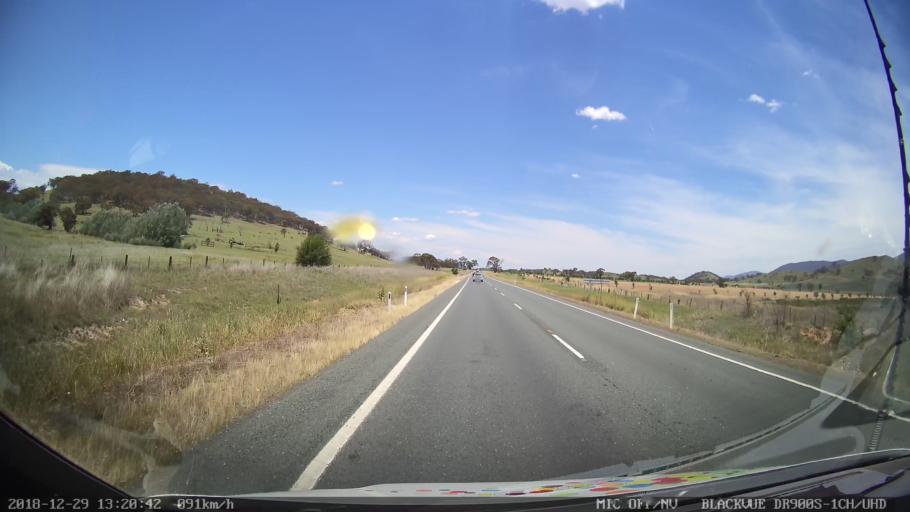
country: AU
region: Australian Capital Territory
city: Macarthur
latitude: -35.7823
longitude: 149.1620
